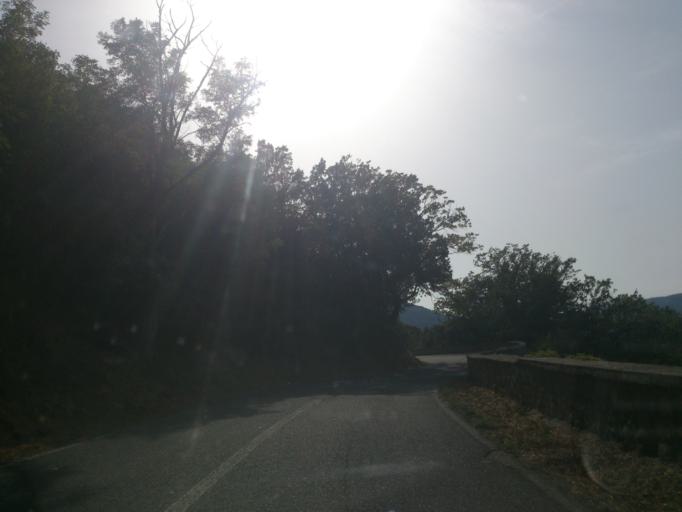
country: IT
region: Calabria
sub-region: Provincia di Reggio Calabria
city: Pazzano
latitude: 38.4673
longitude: 16.4383
